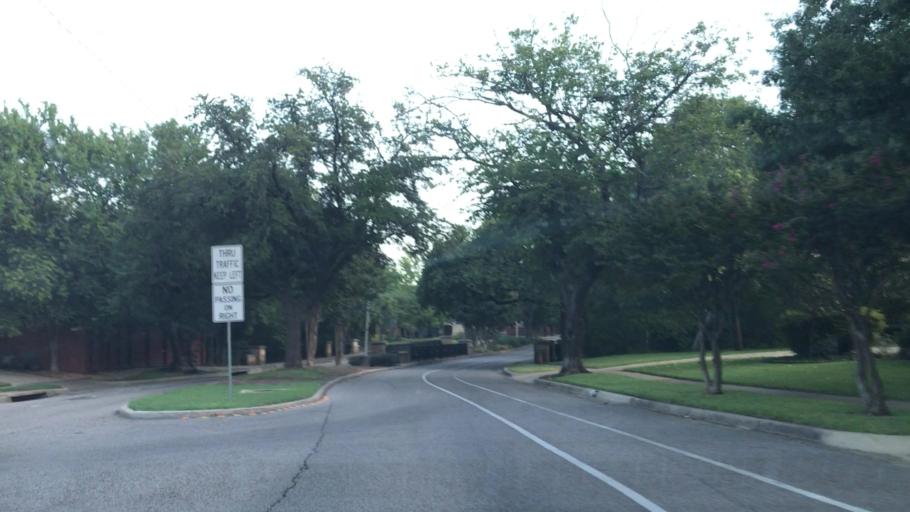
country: US
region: Texas
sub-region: Dallas County
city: Richardson
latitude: 32.9583
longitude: -96.7562
